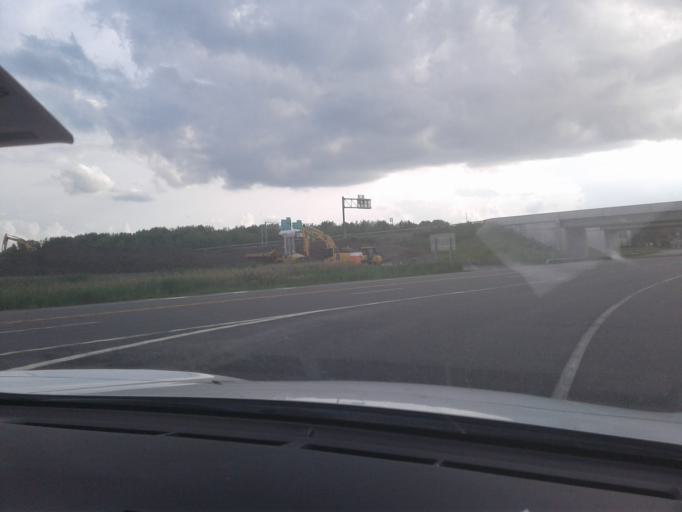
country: US
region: New York
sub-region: Onondaga County
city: East Syracuse
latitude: 43.0779
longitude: -76.0519
